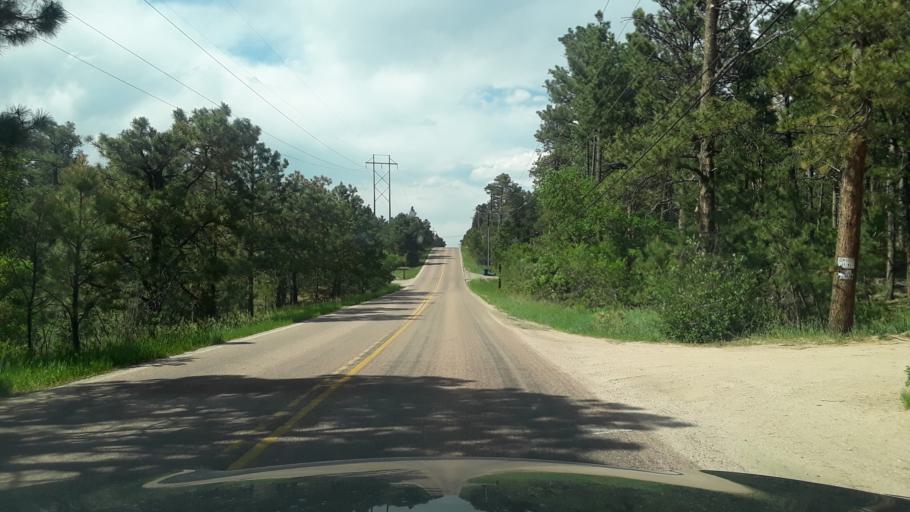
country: US
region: Colorado
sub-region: El Paso County
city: Gleneagle
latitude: 39.0420
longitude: -104.7849
